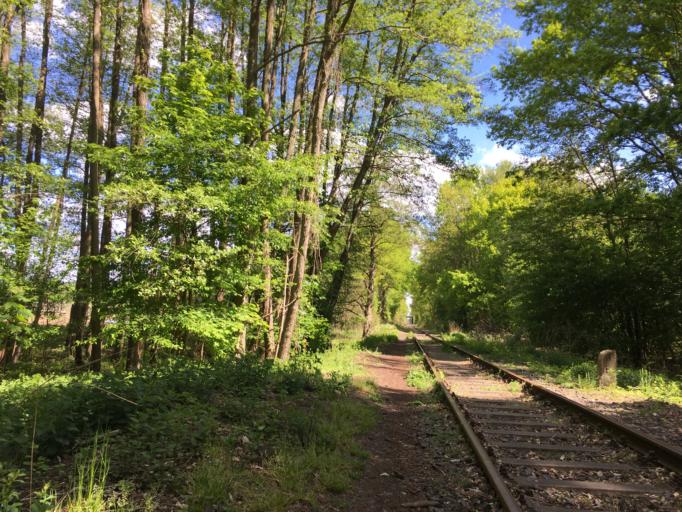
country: DE
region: Berlin
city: Blankenfelde
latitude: 52.6520
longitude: 13.3795
